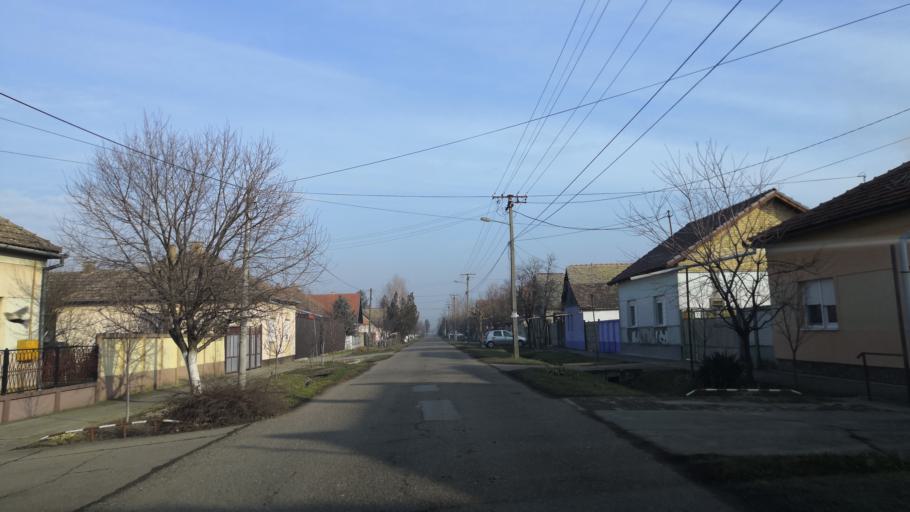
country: RS
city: Kisac
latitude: 45.3462
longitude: 19.7318
